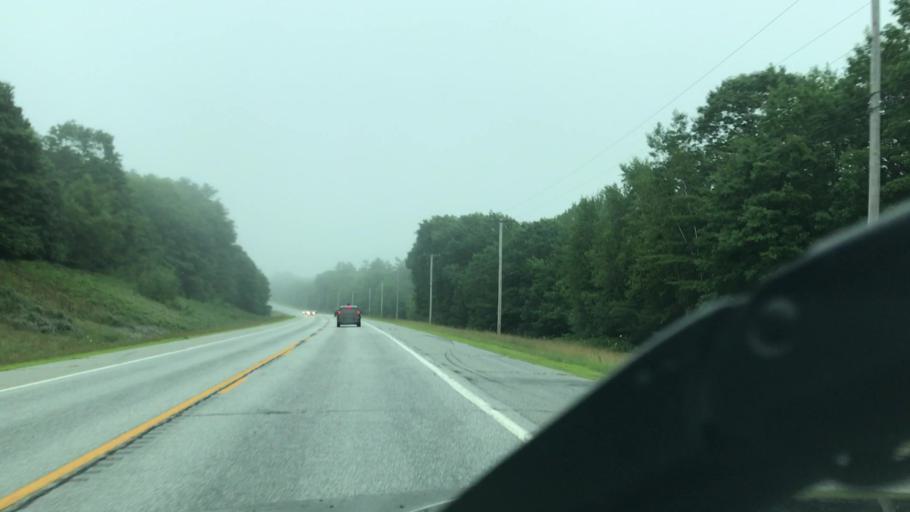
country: US
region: Maine
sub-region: Lincoln County
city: Nobleboro
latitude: 44.0767
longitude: -69.4777
